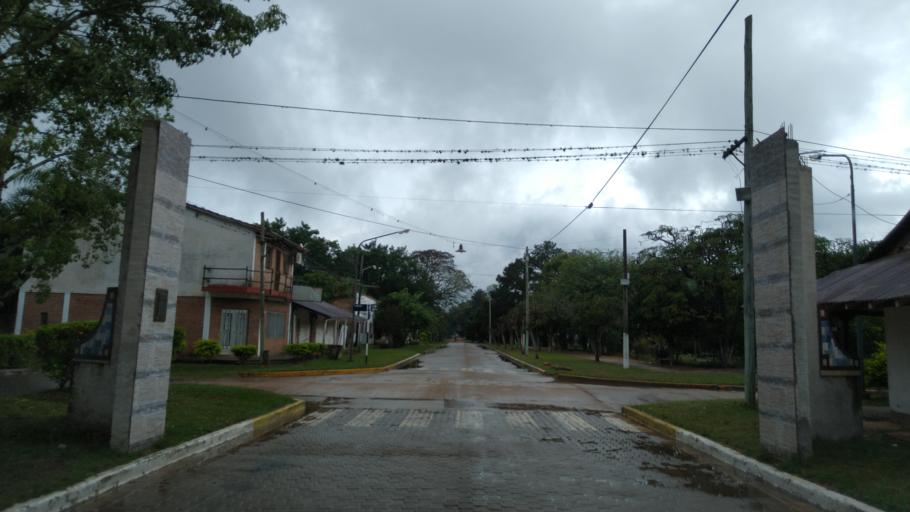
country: AR
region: Corrientes
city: Loreto
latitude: -27.7695
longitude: -57.2803
